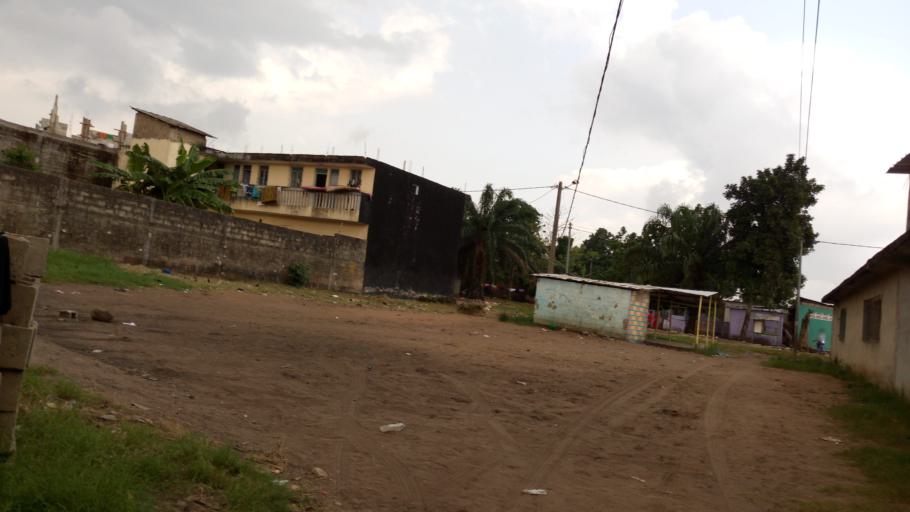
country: CI
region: Lagunes
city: Abobo
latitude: 5.4080
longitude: -3.9965
